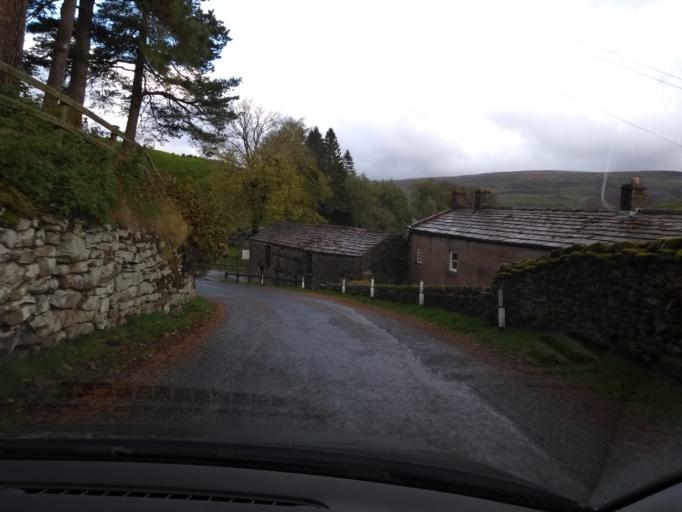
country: GB
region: England
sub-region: Cumbria
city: Kirkby Stephen
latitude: 54.3973
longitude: -2.1724
